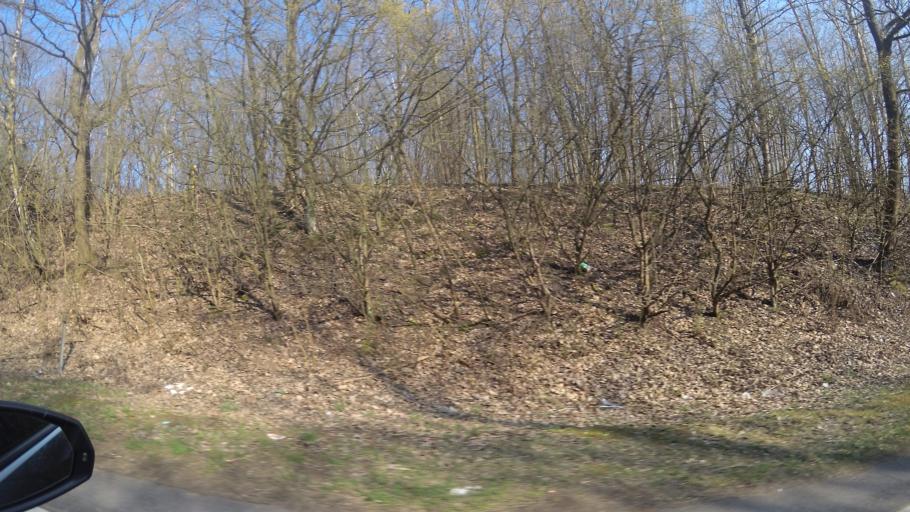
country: DE
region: Saarland
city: Saarbrucken
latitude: 49.2534
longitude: 6.9971
